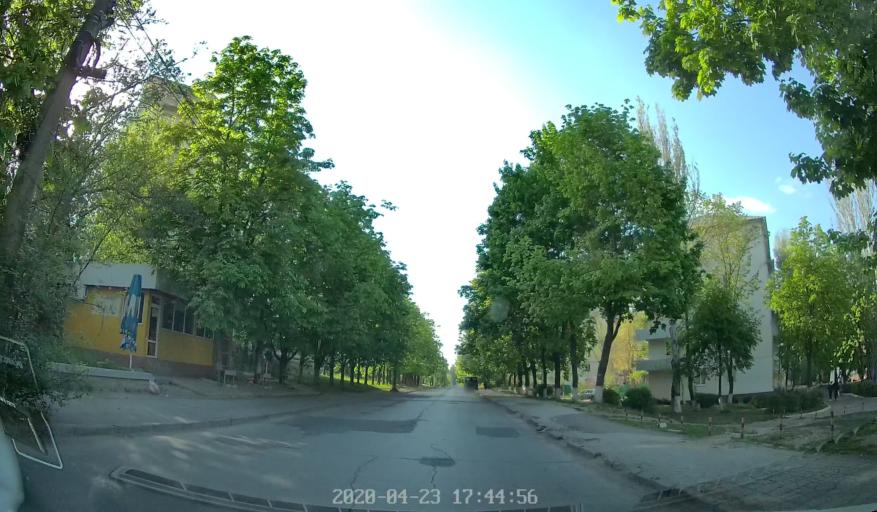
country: MD
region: Chisinau
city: Chisinau
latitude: 46.9934
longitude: 28.8284
